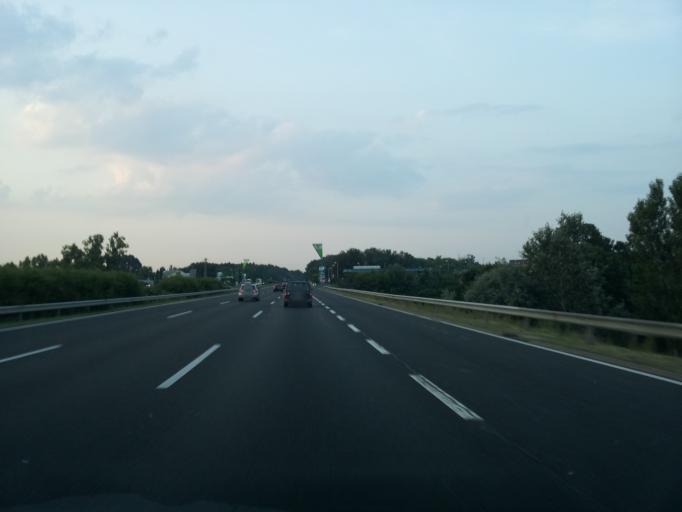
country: HU
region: Fejer
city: Baracska
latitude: 47.3048
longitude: 18.7436
